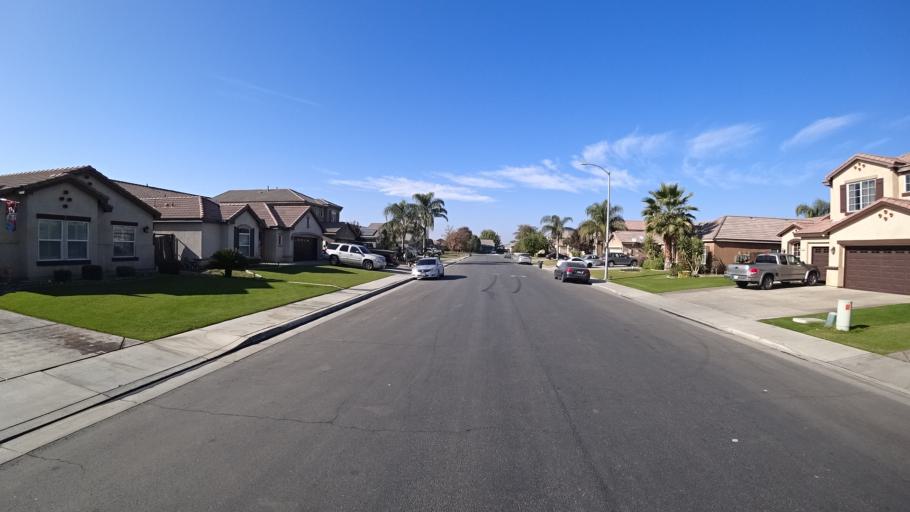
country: US
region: California
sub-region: Kern County
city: Greenfield
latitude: 35.2729
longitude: -119.0603
